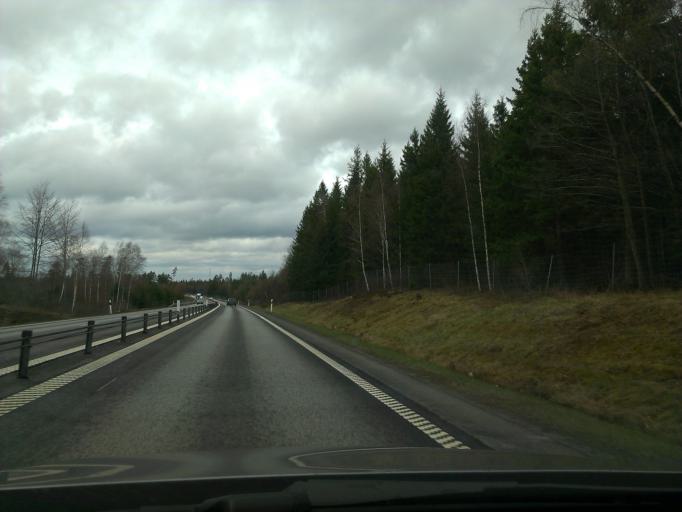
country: SE
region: Kronoberg
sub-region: Almhults Kommun
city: AElmhult
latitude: 56.4646
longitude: 14.1010
